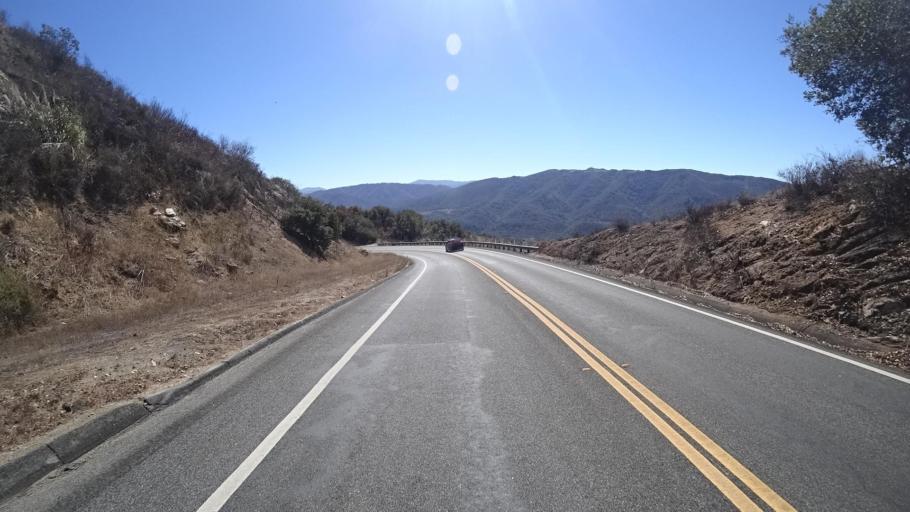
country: US
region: California
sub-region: Monterey County
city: Carmel Valley Village
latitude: 36.5212
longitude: -121.7567
